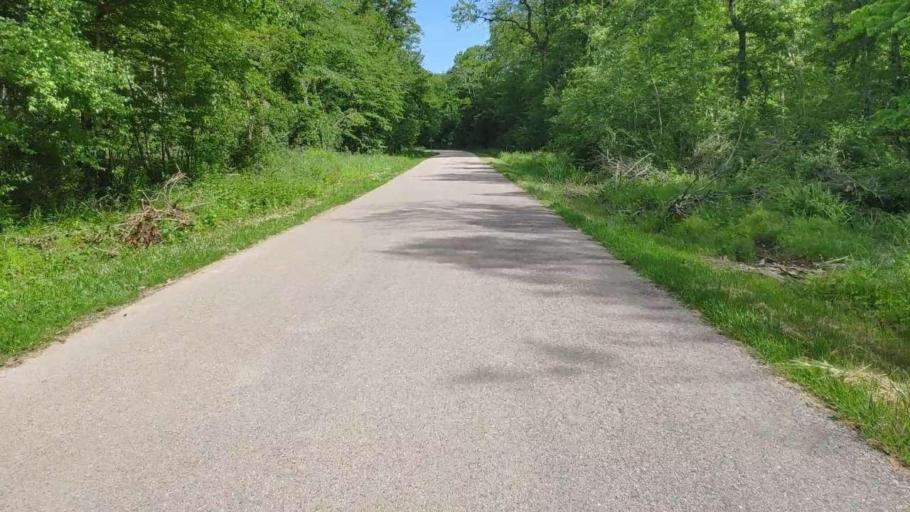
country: FR
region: Franche-Comte
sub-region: Departement du Jura
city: Bletterans
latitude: 46.7158
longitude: 5.3966
